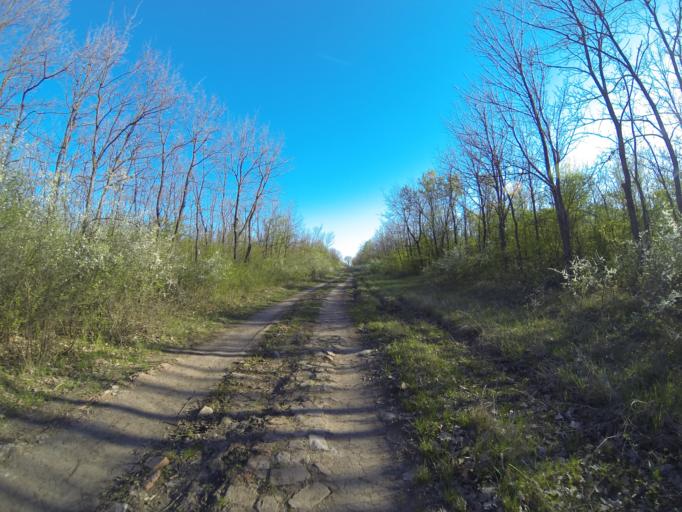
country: RO
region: Dolj
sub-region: Comuna Ceratu
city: Ceratu
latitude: 44.0797
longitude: 23.6820
